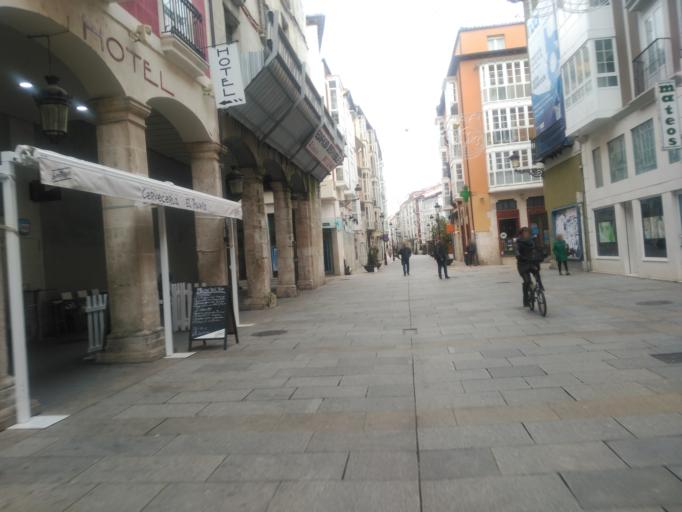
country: ES
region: Castille and Leon
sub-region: Provincia de Burgos
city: Burgos
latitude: 42.3414
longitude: -3.7029
